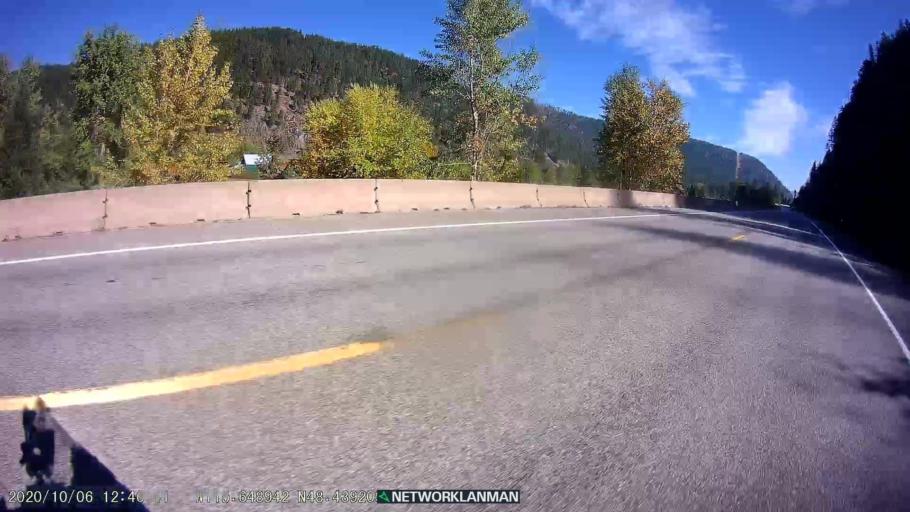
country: US
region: Montana
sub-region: Lincoln County
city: Libby
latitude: 48.4391
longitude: -115.6487
